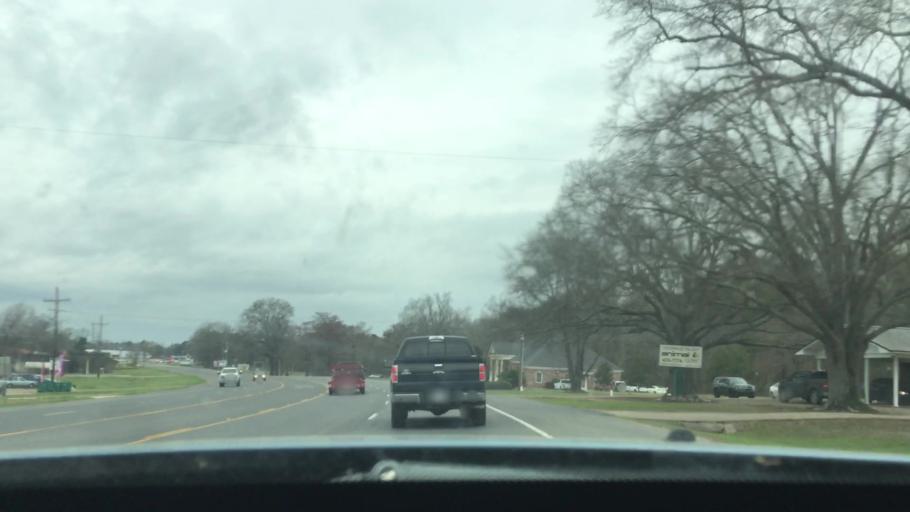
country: US
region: Louisiana
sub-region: Franklin Parish
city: Winnsboro
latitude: 32.1524
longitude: -91.7073
